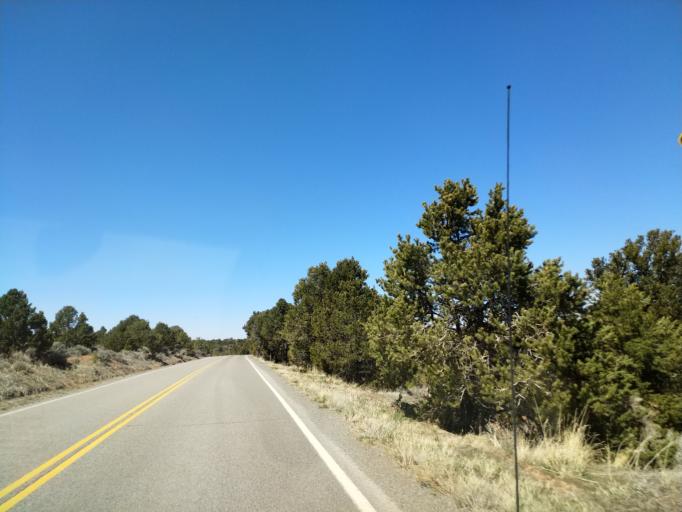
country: US
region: Colorado
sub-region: Mesa County
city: Redlands
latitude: 38.9918
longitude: -108.7693
